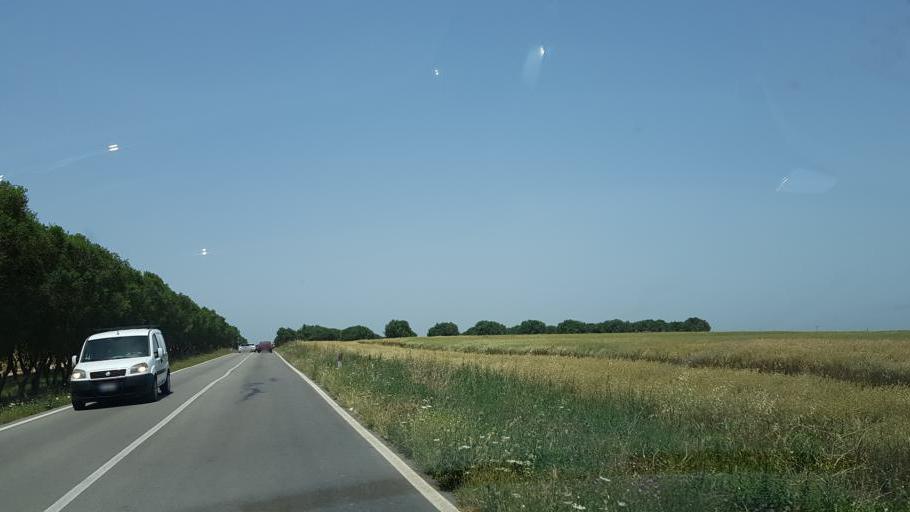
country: IT
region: Apulia
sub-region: Provincia di Brindisi
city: San Pancrazio Salentino
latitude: 40.3672
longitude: 17.8406
